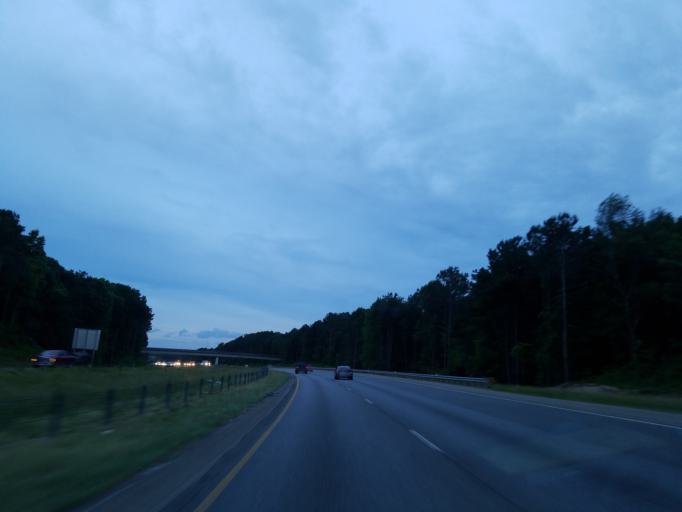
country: US
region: Georgia
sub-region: Cherokee County
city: Holly Springs
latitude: 34.1908
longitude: -84.5054
